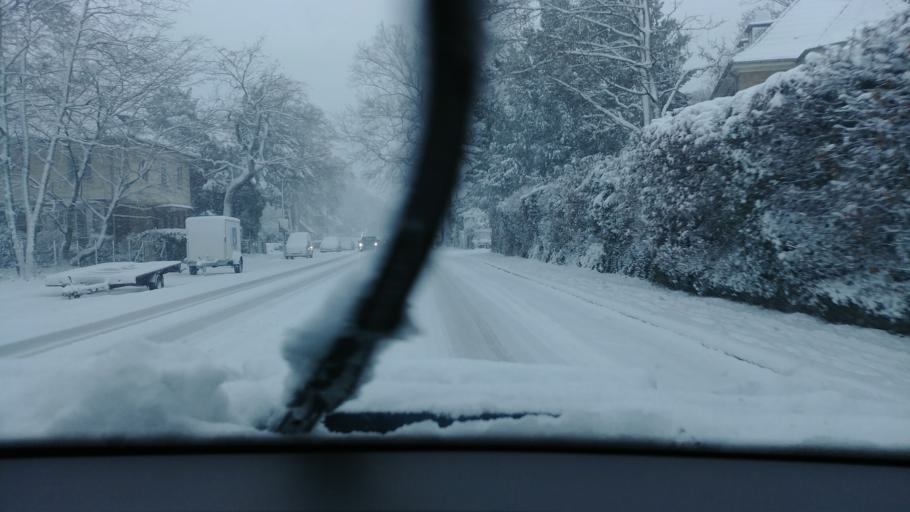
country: DE
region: North Rhine-Westphalia
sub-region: Regierungsbezirk Koln
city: Bergisch Gladbach
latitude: 50.9811
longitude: 7.1288
